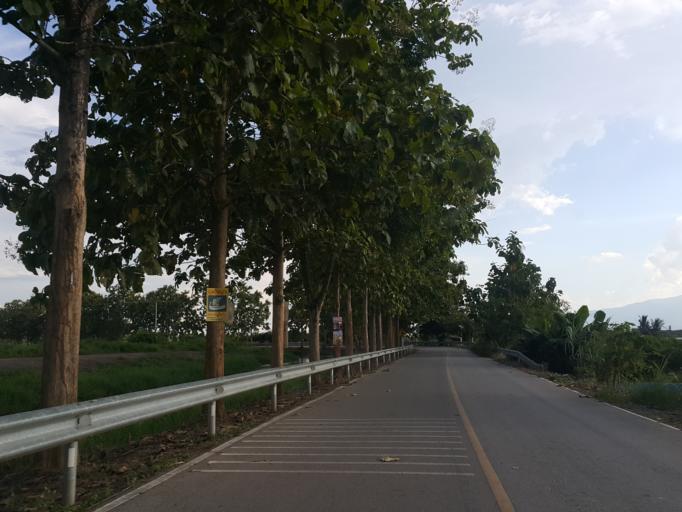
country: TH
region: Chiang Mai
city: Mae Taeng
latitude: 19.0361
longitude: 98.9803
